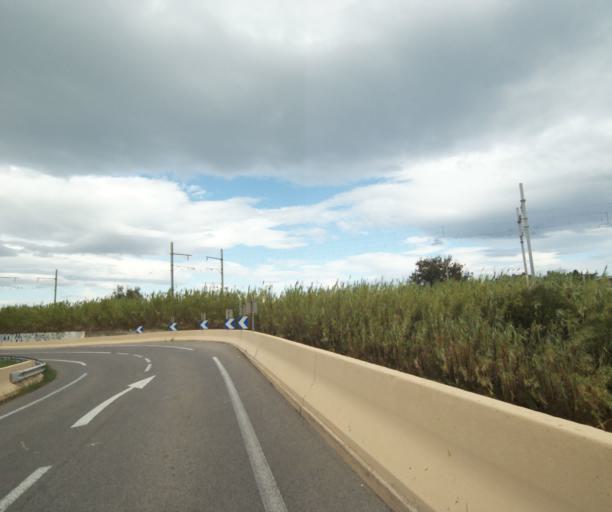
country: FR
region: Languedoc-Roussillon
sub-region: Departement des Pyrenees-Orientales
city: Collioure
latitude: 42.5331
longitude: 3.0672
